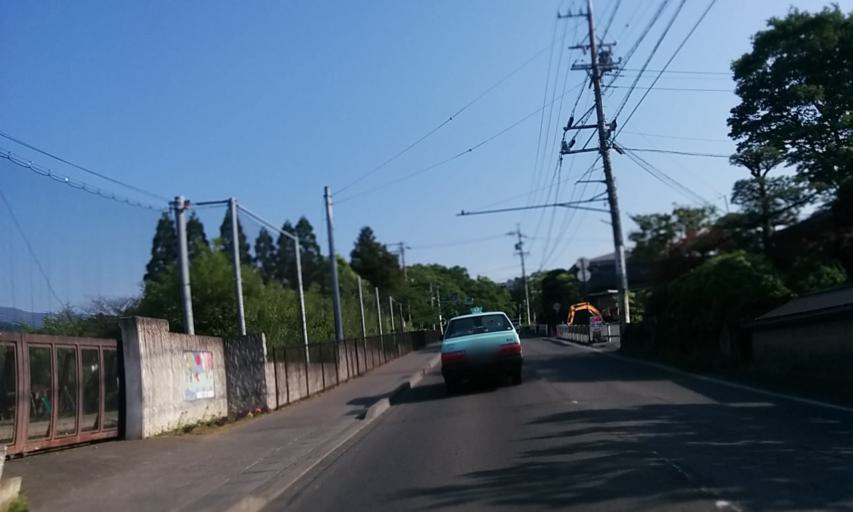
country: JP
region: Nagano
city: Matsumoto
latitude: 36.2283
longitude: 137.9819
